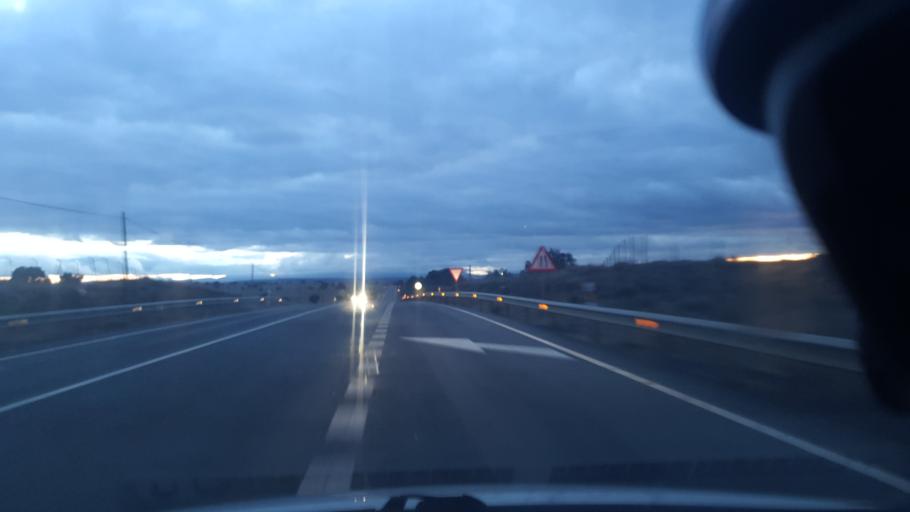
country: ES
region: Castille and Leon
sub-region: Provincia de Avila
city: Mediana de Voltoya
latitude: 40.7150
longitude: -4.5491
